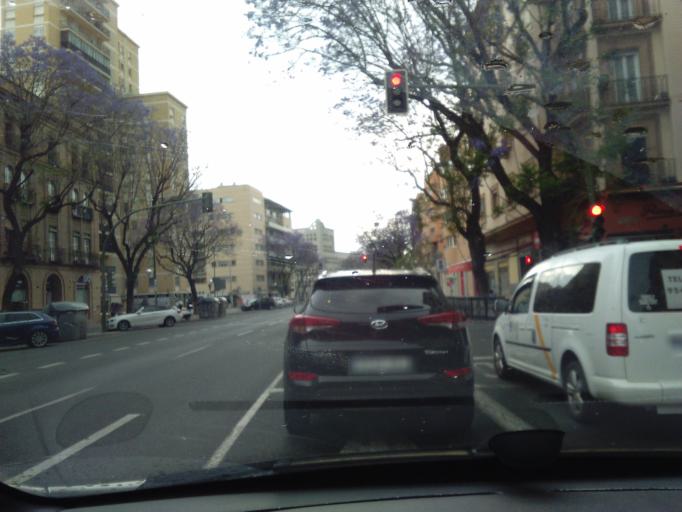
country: ES
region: Andalusia
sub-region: Provincia de Sevilla
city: Sevilla
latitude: 37.3871
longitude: -5.9763
